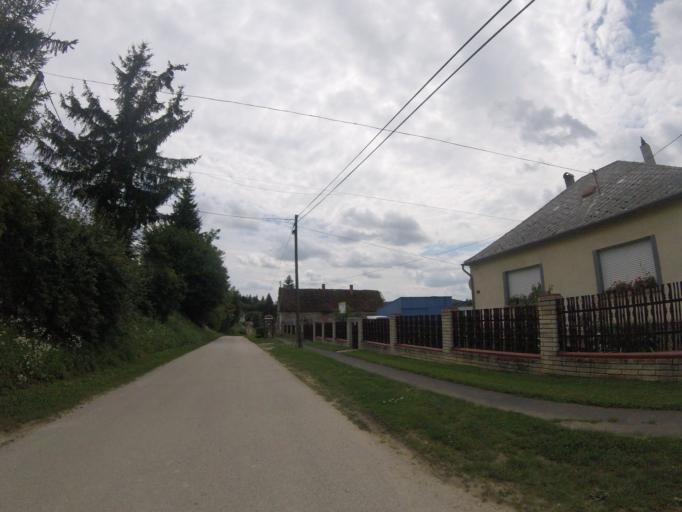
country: HU
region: Zala
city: Nagykanizsa
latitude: 46.5557
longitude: 17.0445
